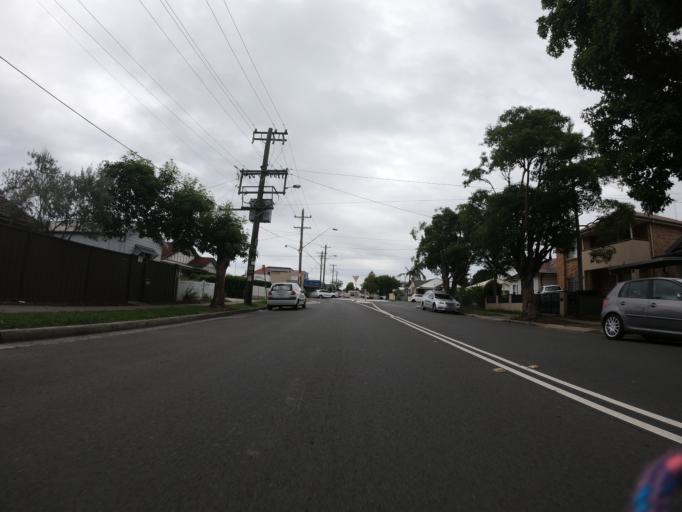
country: AU
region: New South Wales
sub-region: Parramatta
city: Granville
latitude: -33.8402
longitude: 151.0057
